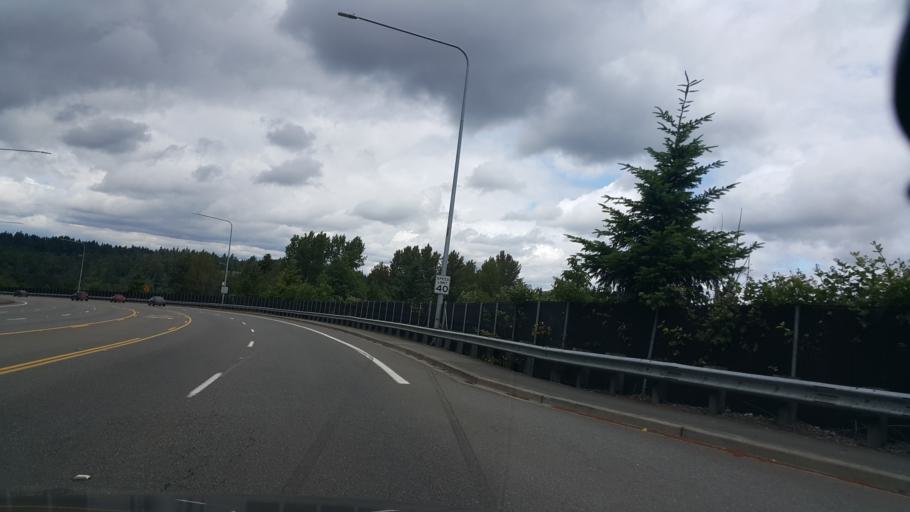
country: US
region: Washington
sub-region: King County
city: Fairwood
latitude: 47.4617
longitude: -122.1467
